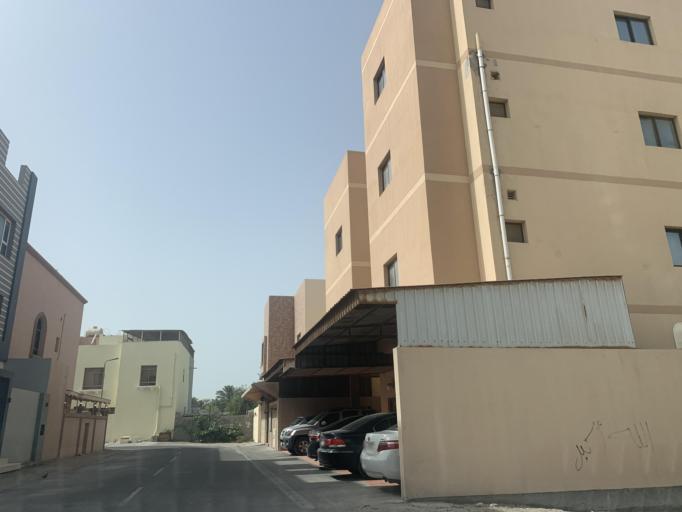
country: BH
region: Northern
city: Sitrah
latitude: 26.1712
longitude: 50.6237
